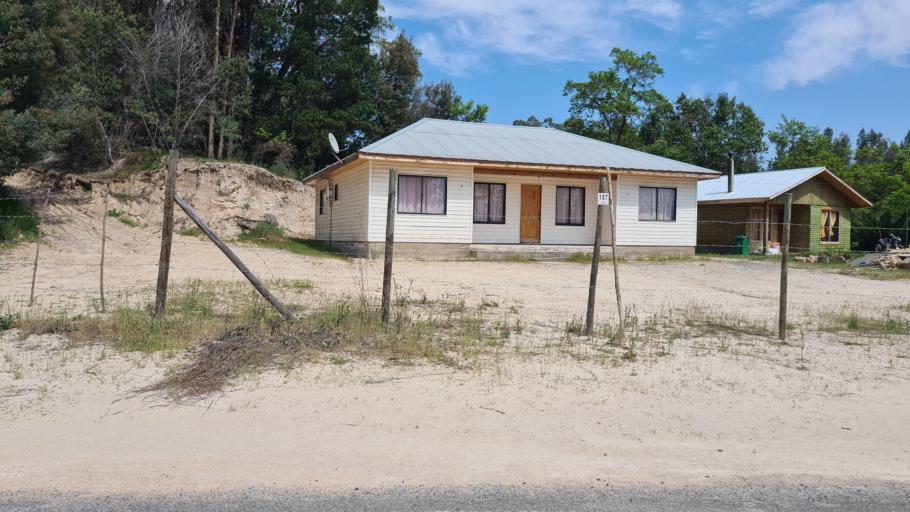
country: CL
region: O'Higgins
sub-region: Provincia de Cachapoal
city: San Vicente
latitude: -34.1576
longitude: -71.4170
